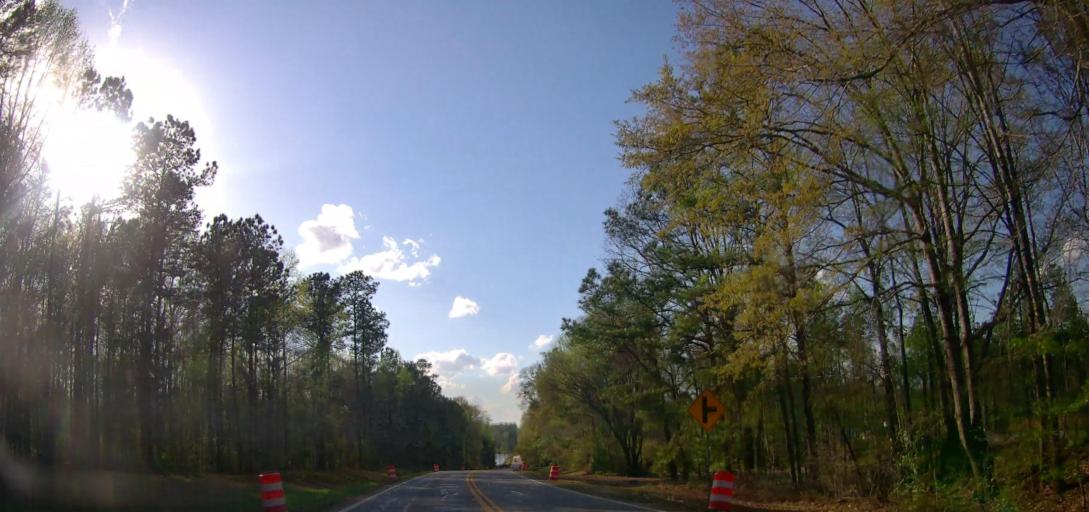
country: US
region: Georgia
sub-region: Baldwin County
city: Milledgeville
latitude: 33.1605
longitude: -83.3690
